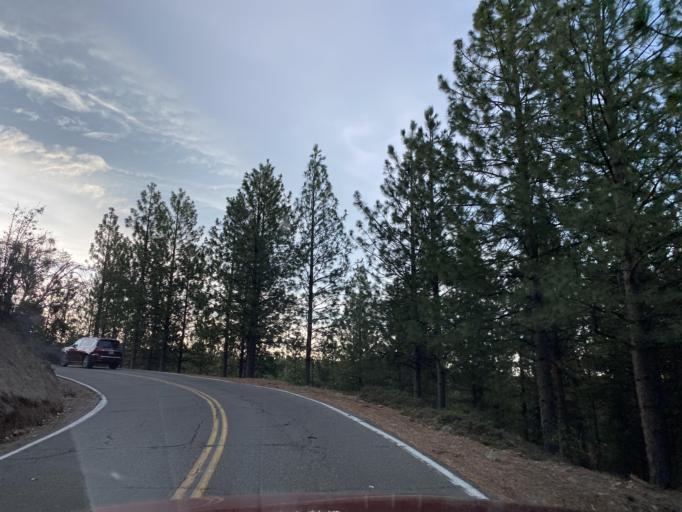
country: US
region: California
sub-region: Amador County
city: Pioneer
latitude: 38.4970
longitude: -120.5950
